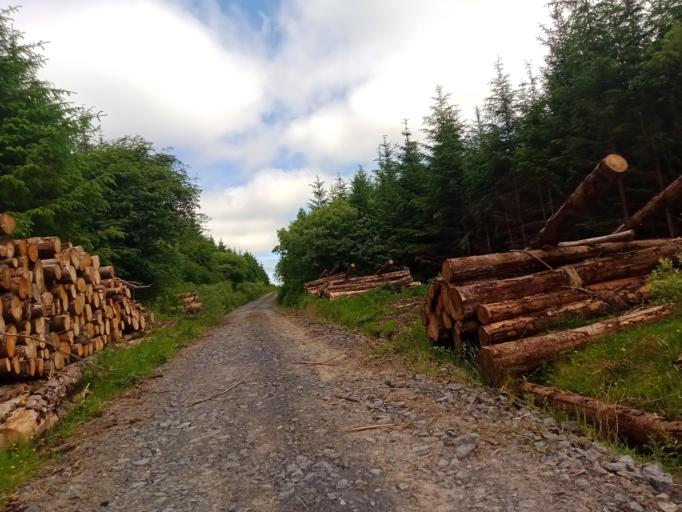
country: IE
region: Leinster
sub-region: Kilkenny
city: Ballyragget
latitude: 52.7884
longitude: -7.4468
